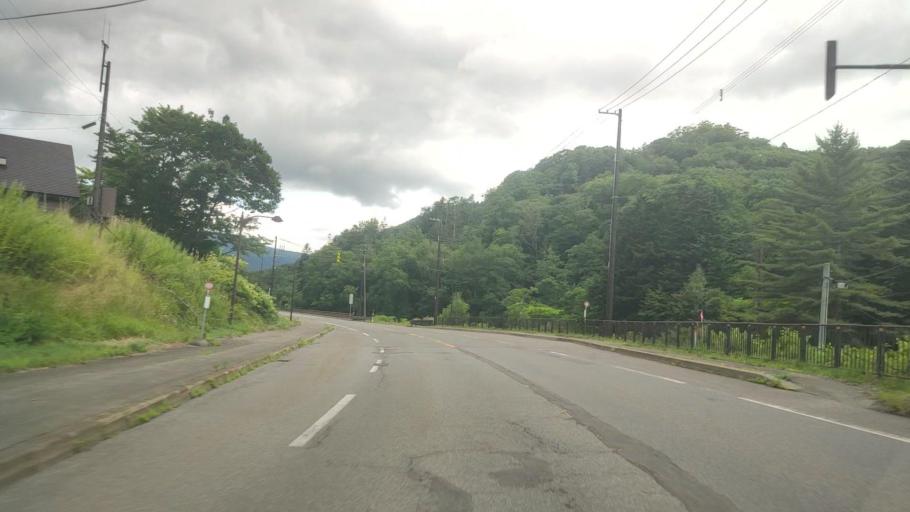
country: JP
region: Hokkaido
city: Date
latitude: 42.6148
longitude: 141.0232
